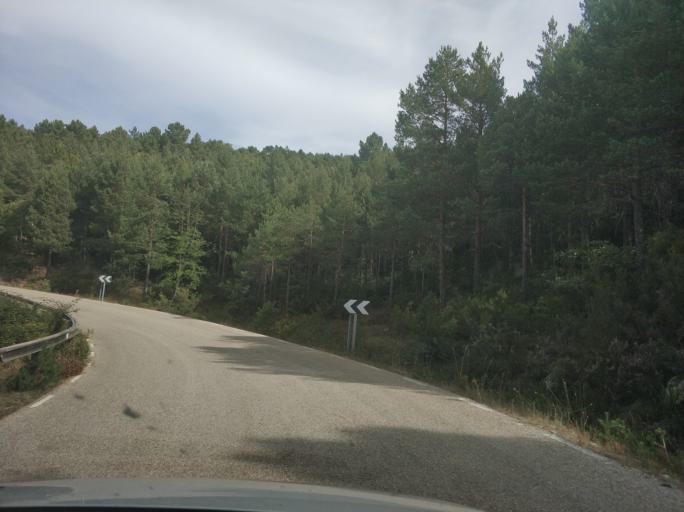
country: ES
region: Castille and Leon
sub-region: Provincia de Soria
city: Duruelo de la Sierra
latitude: 41.9004
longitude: -2.9392
